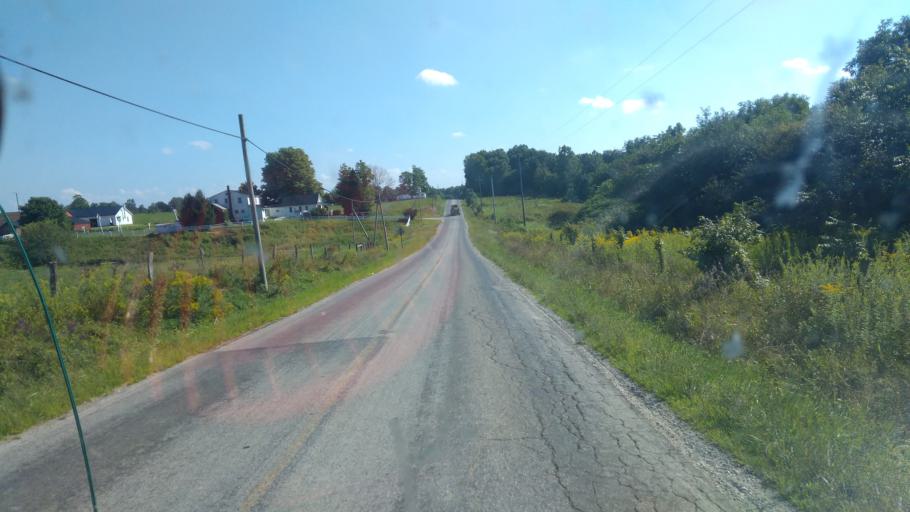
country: US
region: Ohio
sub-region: Ashland County
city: Ashland
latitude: 40.9091
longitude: -82.4359
